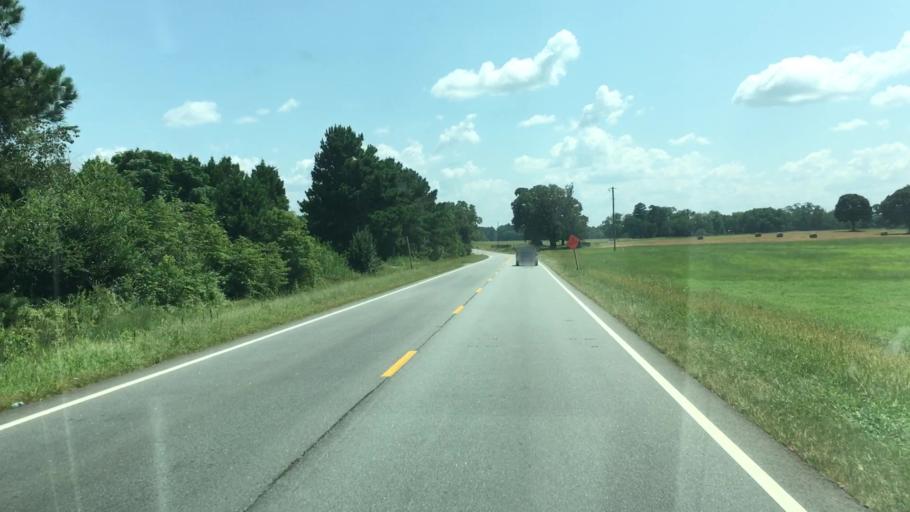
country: US
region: Georgia
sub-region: Oconee County
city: Watkinsville
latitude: 33.8033
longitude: -83.4270
